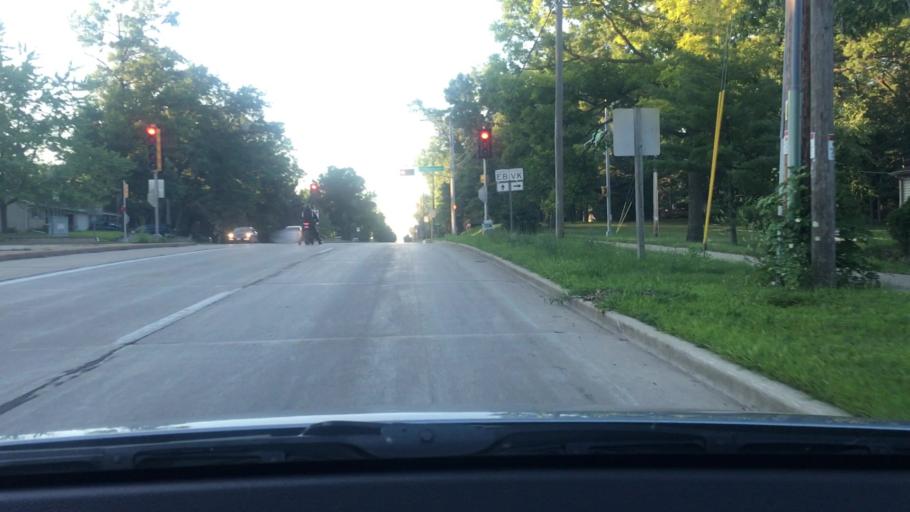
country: US
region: Wisconsin
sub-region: Brown County
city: Howard
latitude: 44.5089
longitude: -88.0993
